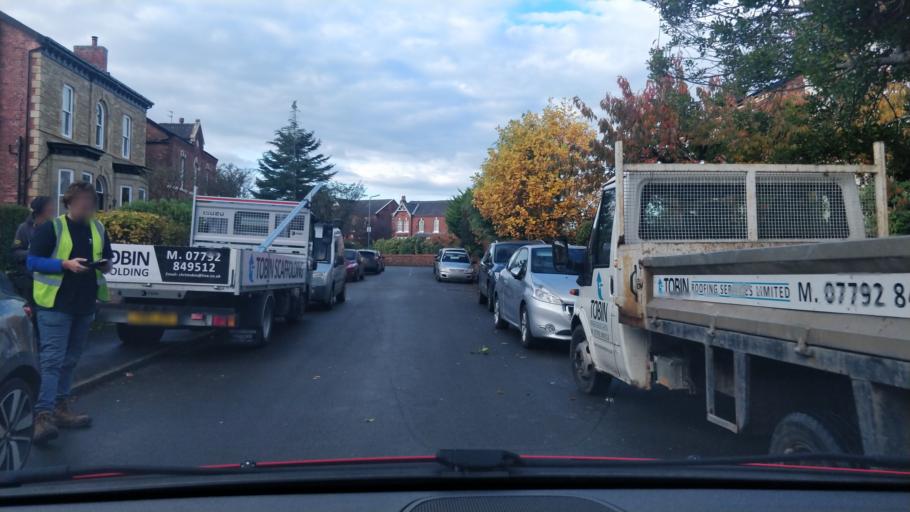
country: GB
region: England
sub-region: Sefton
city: Southport
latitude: 53.6307
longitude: -3.0163
